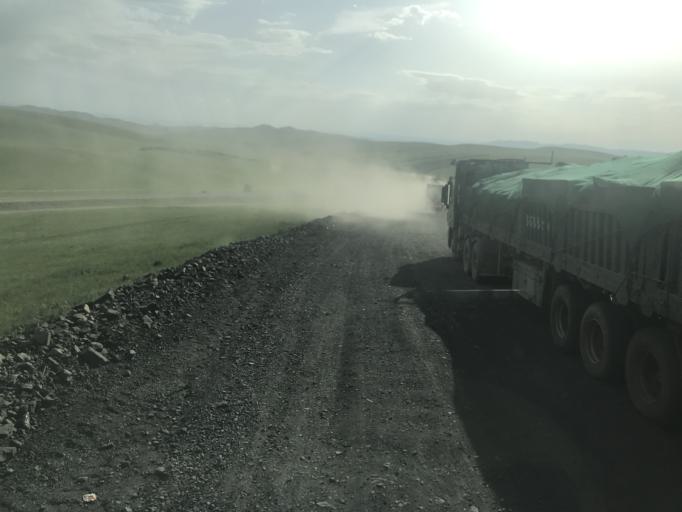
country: MN
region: Central Aimak
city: Javhlant
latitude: 48.6493
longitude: 106.0967
